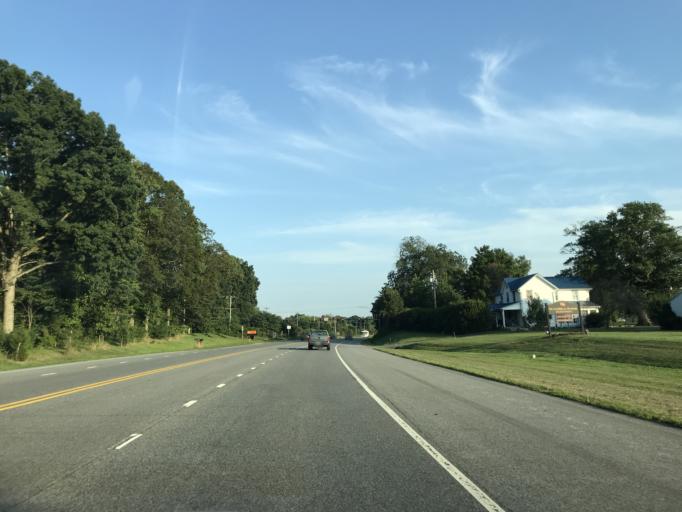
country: US
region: Maryland
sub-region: Cecil County
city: Rising Sun
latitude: 39.6914
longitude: -75.9746
